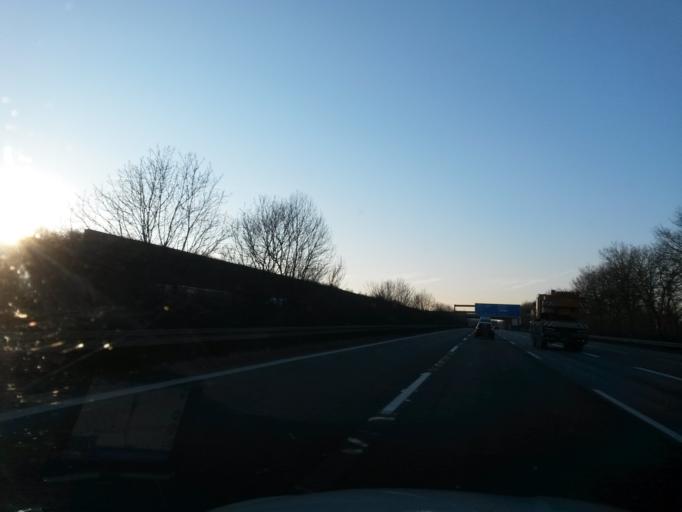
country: DE
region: Bavaria
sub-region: Upper Bavaria
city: Kirchheim bei Muenchen
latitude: 48.1631
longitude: 11.7443
